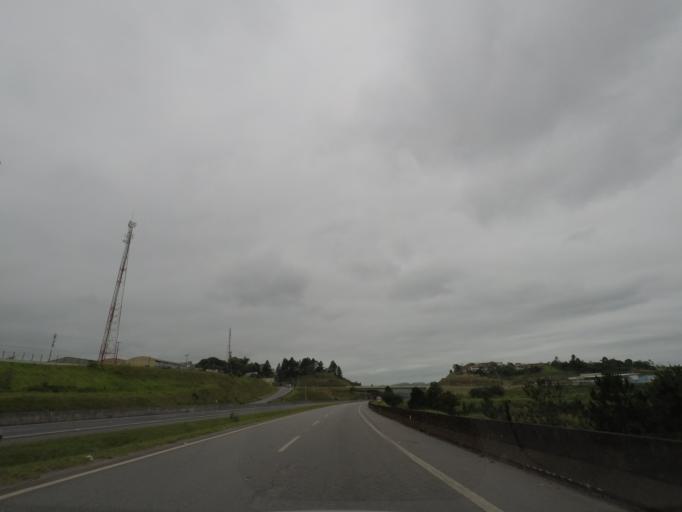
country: BR
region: Sao Paulo
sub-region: Santa Isabel
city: Santa Isabel
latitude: -23.2046
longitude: -46.1613
